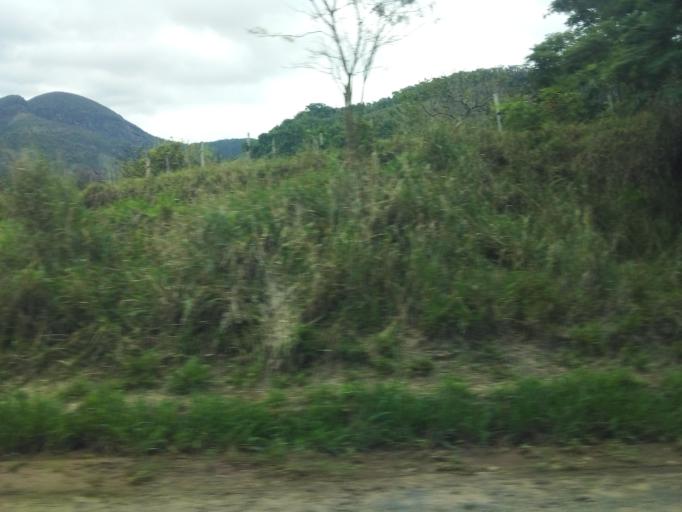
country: BR
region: Minas Gerais
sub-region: Nova Era
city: Nova Era
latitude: -19.6756
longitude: -42.8953
